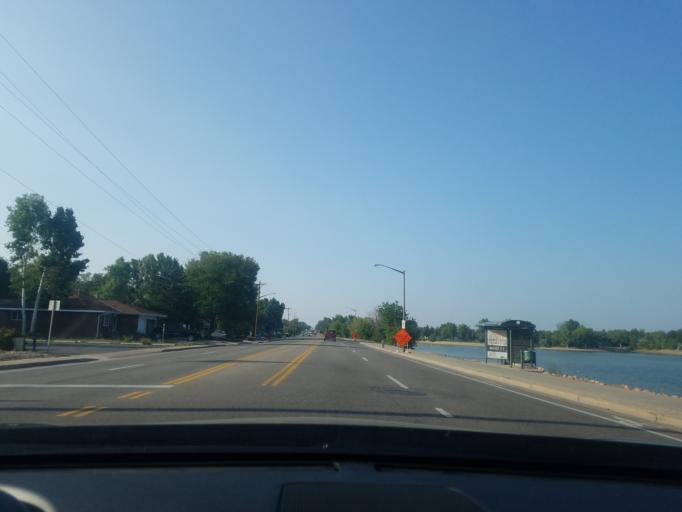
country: US
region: Colorado
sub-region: Larimer County
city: Loveland
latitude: 40.4145
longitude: -105.0969
